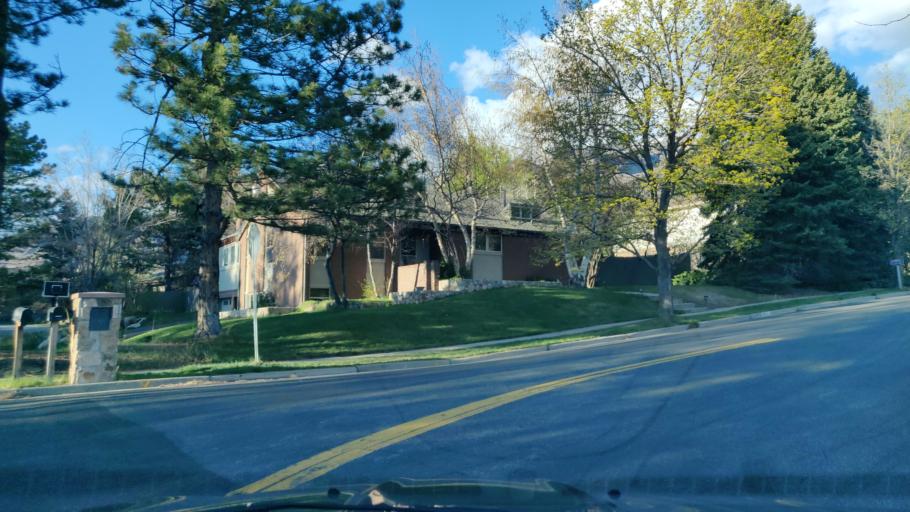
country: US
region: Utah
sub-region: Salt Lake County
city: Cottonwood Heights
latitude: 40.6155
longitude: -111.7959
